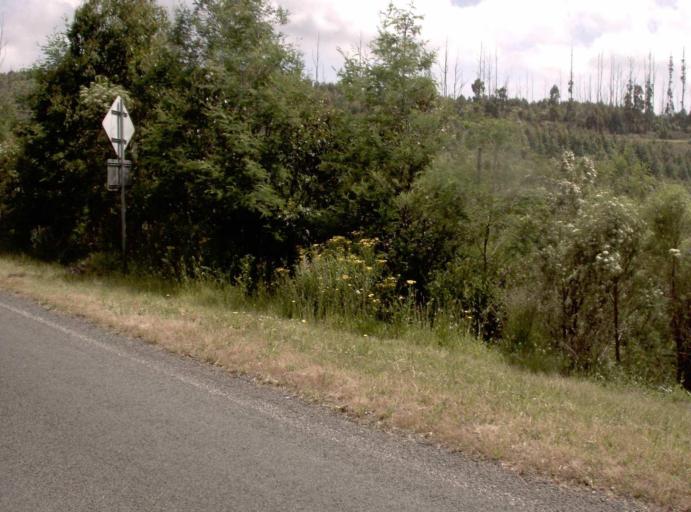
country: AU
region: Victoria
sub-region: Latrobe
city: Traralgon
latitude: -38.3589
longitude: 146.5674
